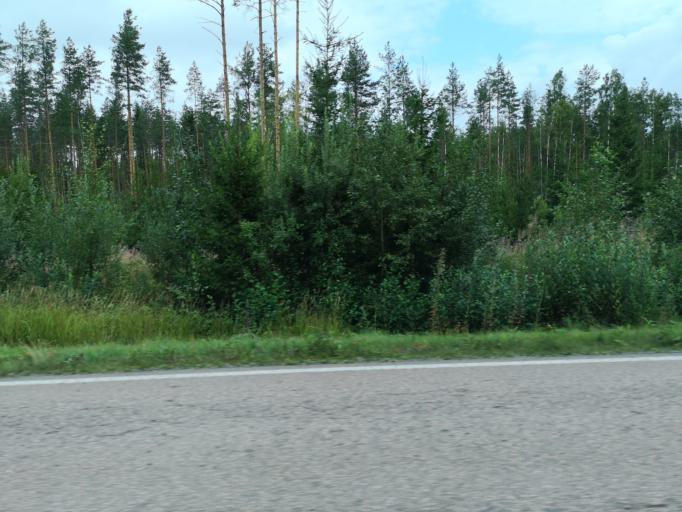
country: FI
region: Central Finland
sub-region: Jyvaeskylae
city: Hankasalmi
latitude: 62.3574
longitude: 26.4957
